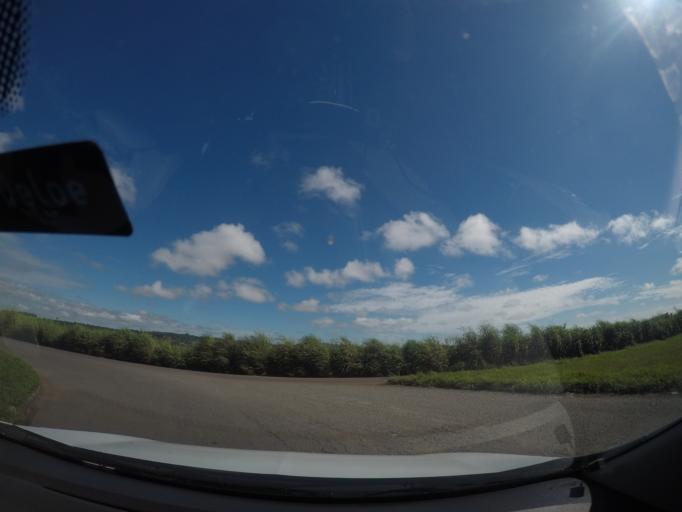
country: BR
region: Goias
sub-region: Senador Canedo
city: Senador Canedo
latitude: -16.6491
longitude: -49.1560
